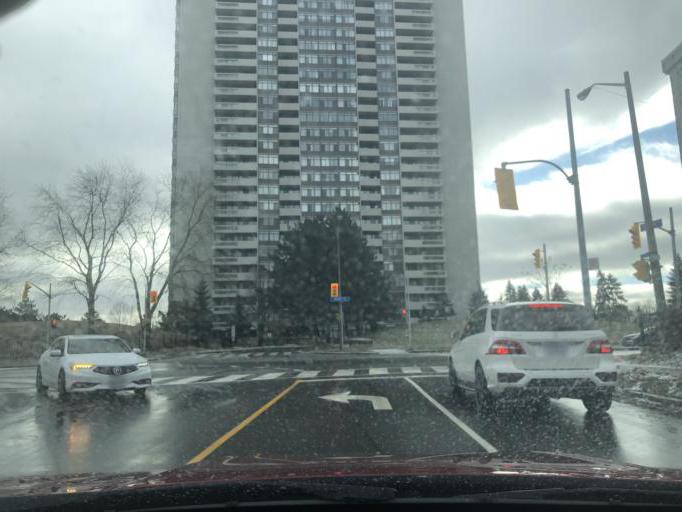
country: CA
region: Ontario
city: Willowdale
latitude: 43.7937
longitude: -79.3524
